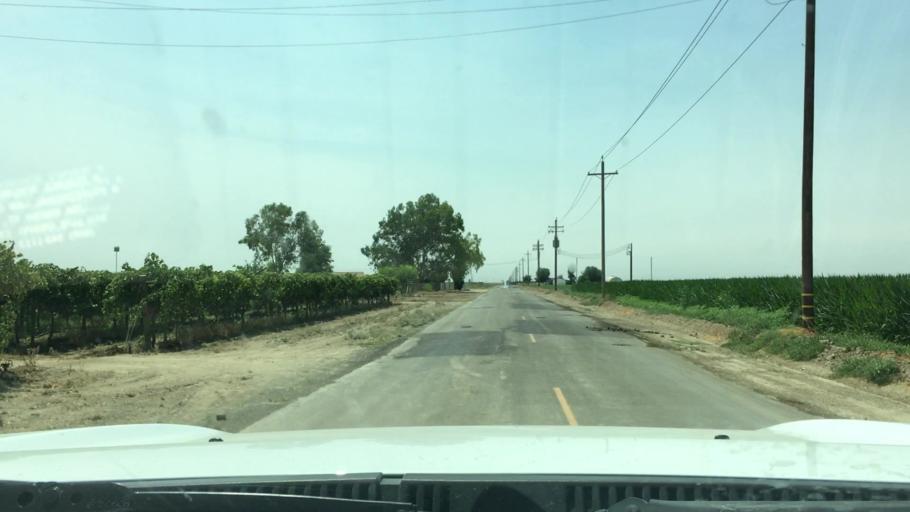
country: US
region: California
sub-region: Tulare County
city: Alpaugh
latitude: 35.7376
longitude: -119.4371
